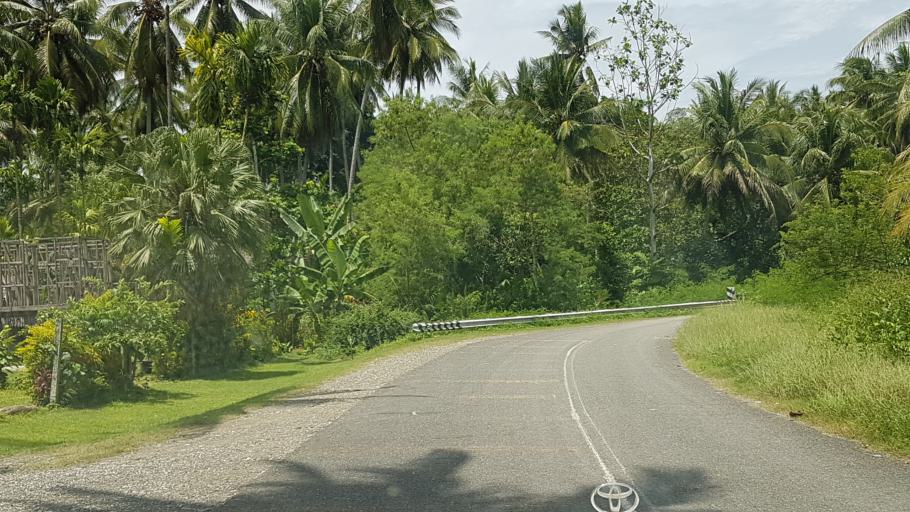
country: PG
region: Madang
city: Madang
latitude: -4.5025
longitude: 145.4183
